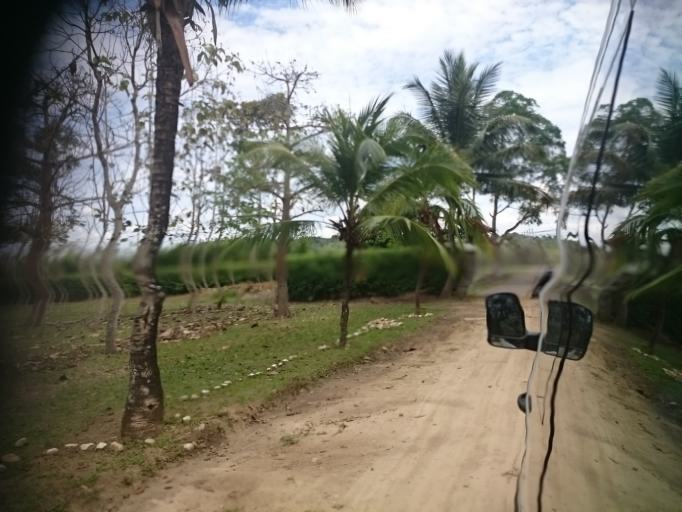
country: PE
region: San Martin
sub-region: Provincia de San Martin
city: Tarapoto
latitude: -6.5117
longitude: -76.3438
